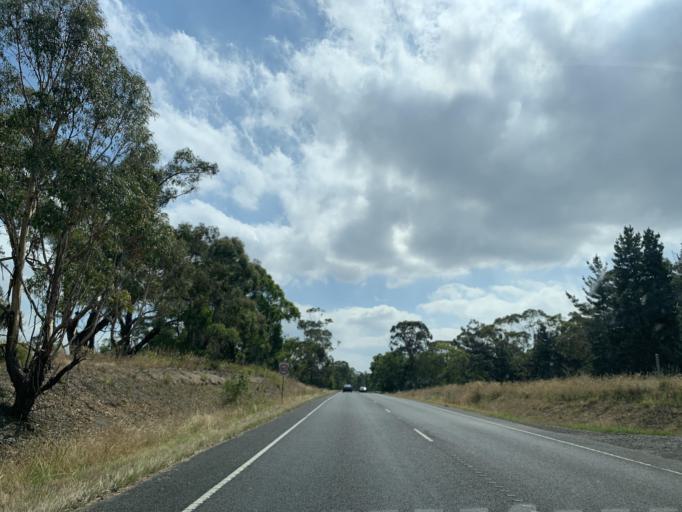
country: AU
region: Victoria
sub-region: Latrobe
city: Morwell
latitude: -38.2038
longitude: 146.4594
